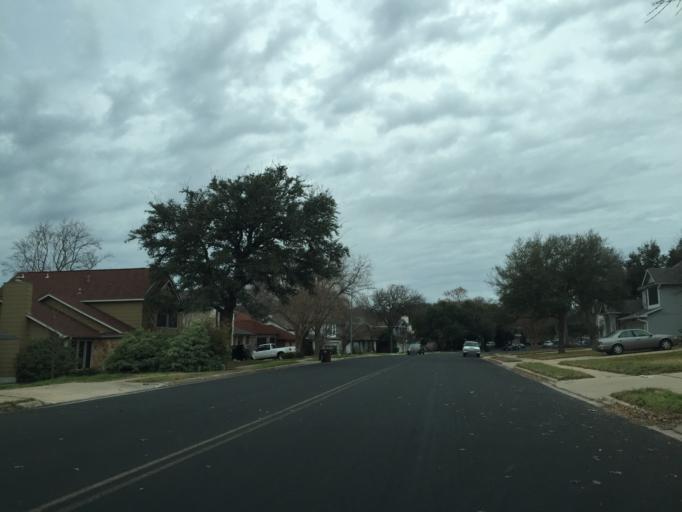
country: US
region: Texas
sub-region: Williamson County
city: Jollyville
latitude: 30.4461
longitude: -97.7455
